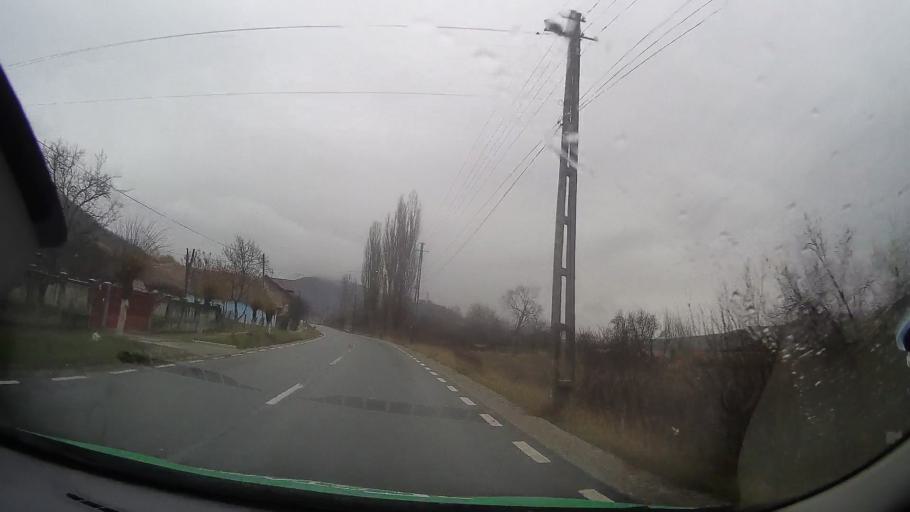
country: RO
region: Bistrita-Nasaud
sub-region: Comuna Galatii Bistritei
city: Galatii Bistritei
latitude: 46.9849
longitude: 24.4275
